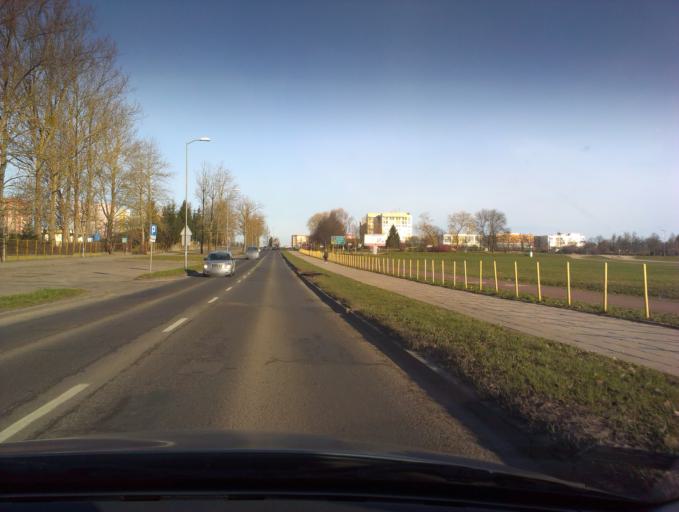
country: PL
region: West Pomeranian Voivodeship
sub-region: Koszalin
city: Koszalin
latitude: 54.1990
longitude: 16.2016
